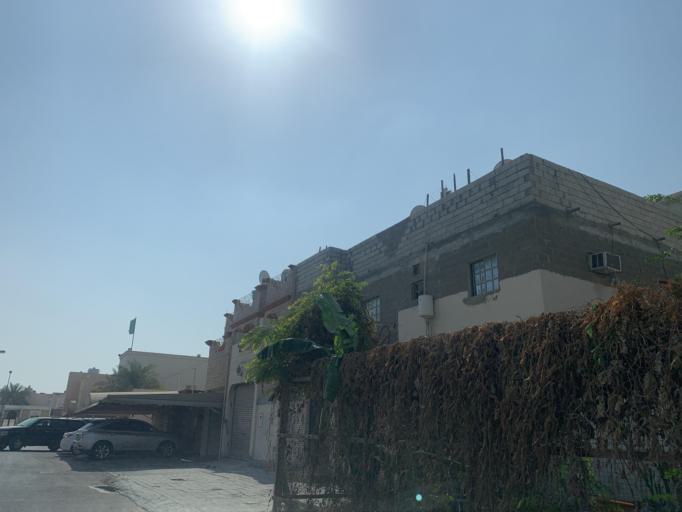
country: BH
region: Central Governorate
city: Madinat Hamad
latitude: 26.1305
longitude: 50.4947
